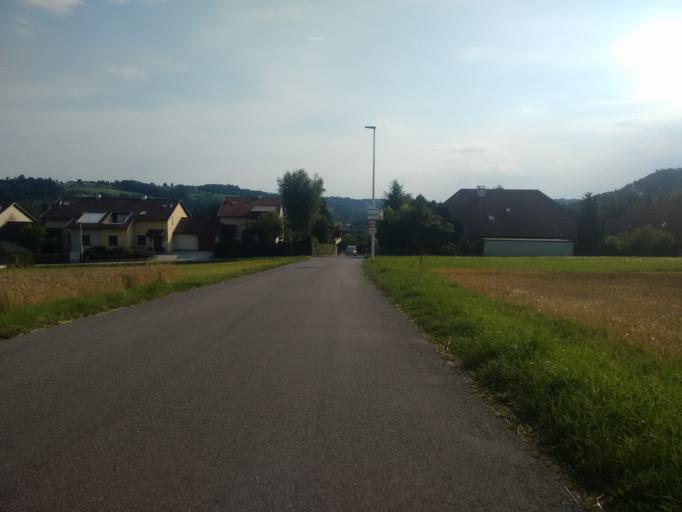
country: AT
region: Upper Austria
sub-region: Politischer Bezirk Grieskirchen
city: Bad Schallerbach
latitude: 48.2357
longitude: 13.9255
